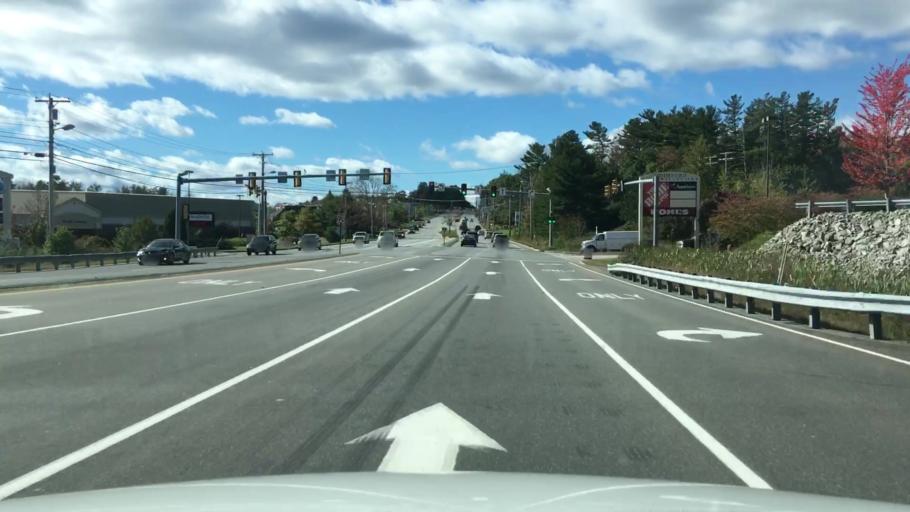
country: US
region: Maine
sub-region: York County
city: Biddeford
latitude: 43.4768
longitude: -70.5053
